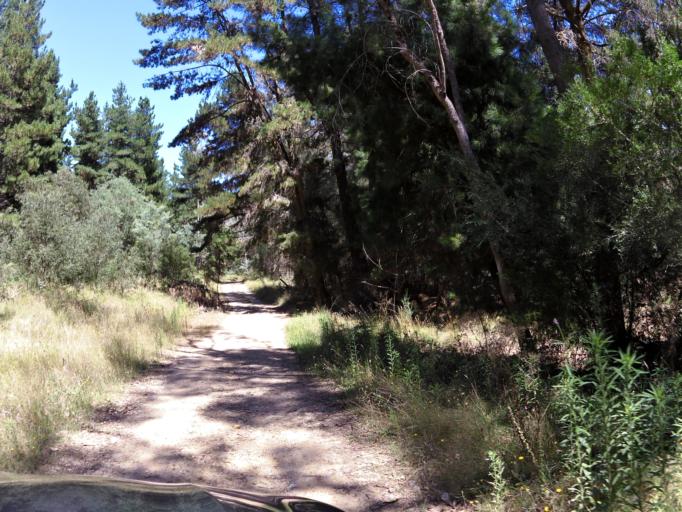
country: AU
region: Victoria
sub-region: Alpine
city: Mount Beauty
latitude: -36.7270
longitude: 146.9852
